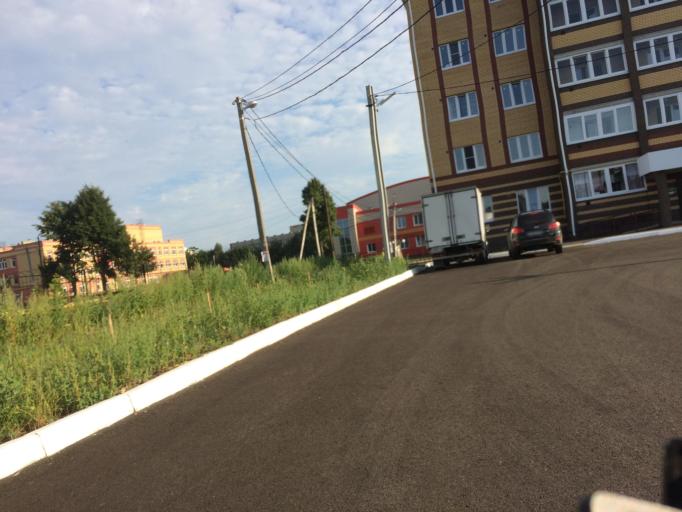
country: RU
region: Mariy-El
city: Medvedevo
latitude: 56.6351
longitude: 47.8107
